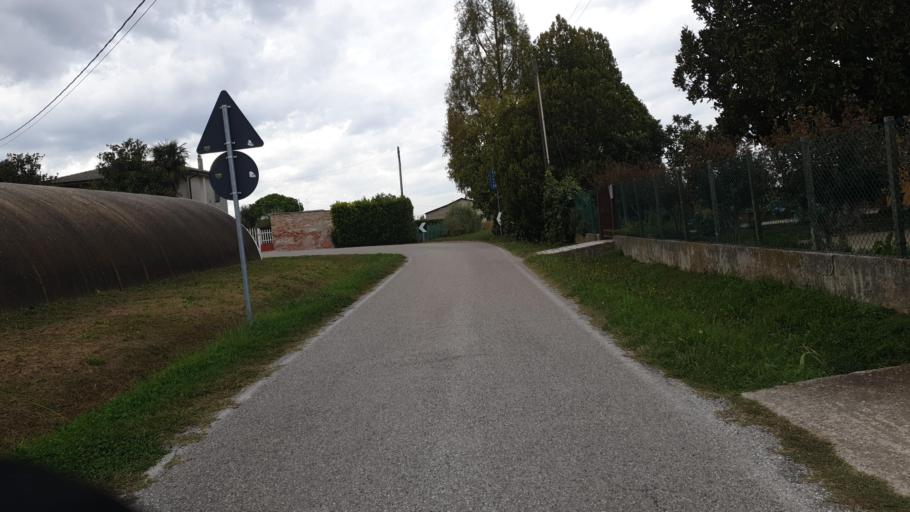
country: IT
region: Veneto
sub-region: Provincia di Padova
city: Bovolenta
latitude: 45.2834
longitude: 11.9461
